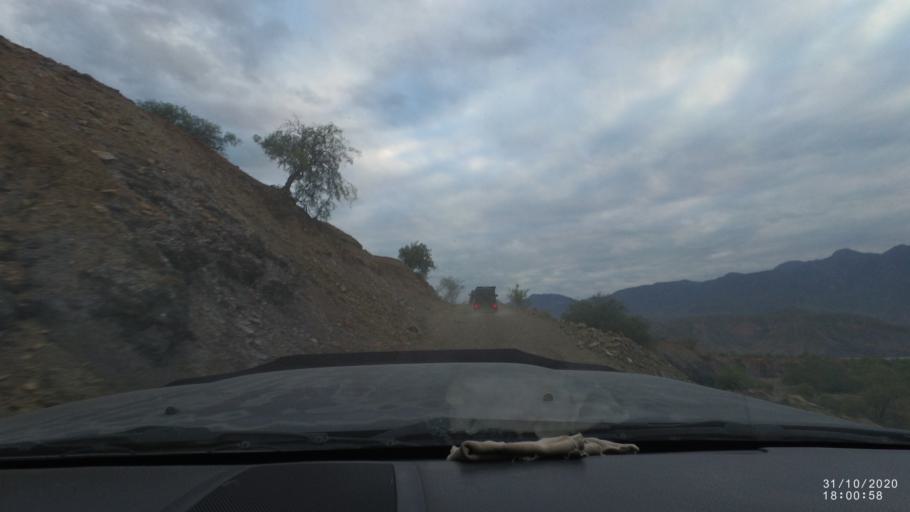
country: BO
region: Chuquisaca
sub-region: Provincia Zudanez
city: Mojocoya
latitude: -18.6646
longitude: -64.5323
